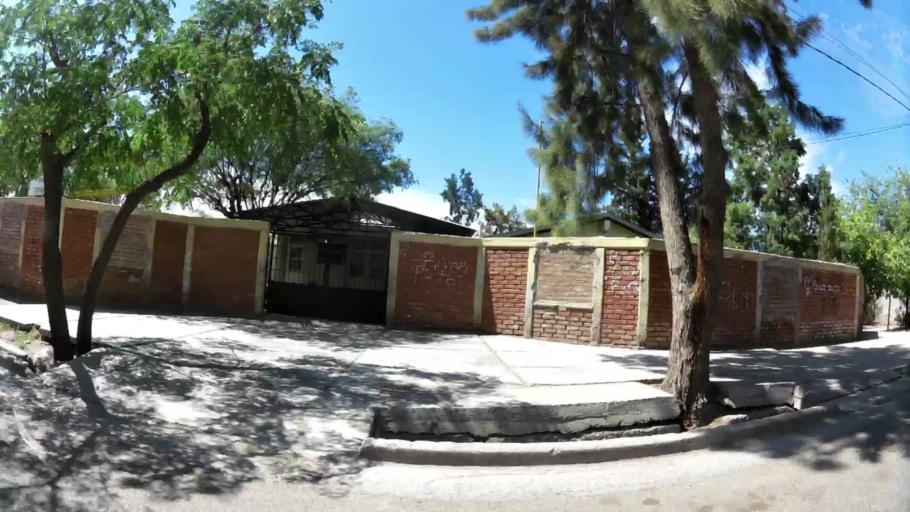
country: AR
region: Mendoza
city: Las Heras
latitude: -32.8639
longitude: -68.8641
